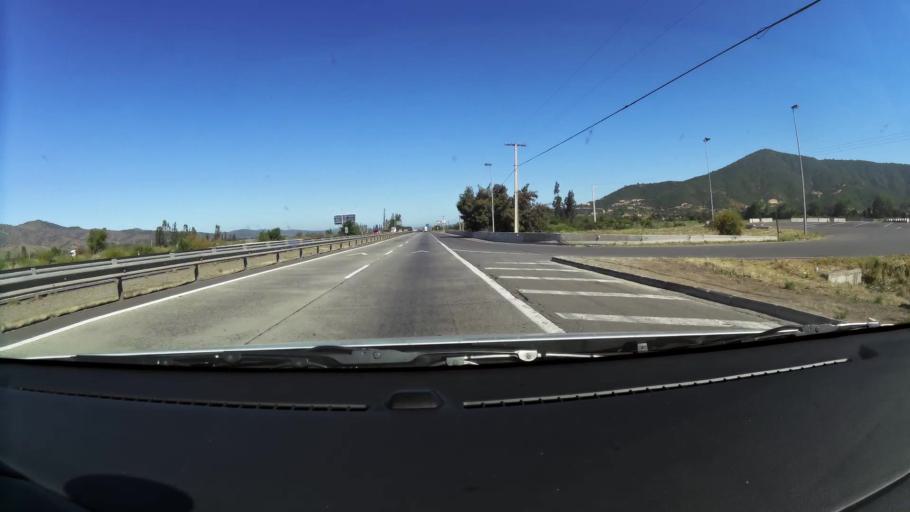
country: CL
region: Valparaiso
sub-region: Provincia de Marga Marga
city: Villa Alemana
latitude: -33.3380
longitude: -71.3718
